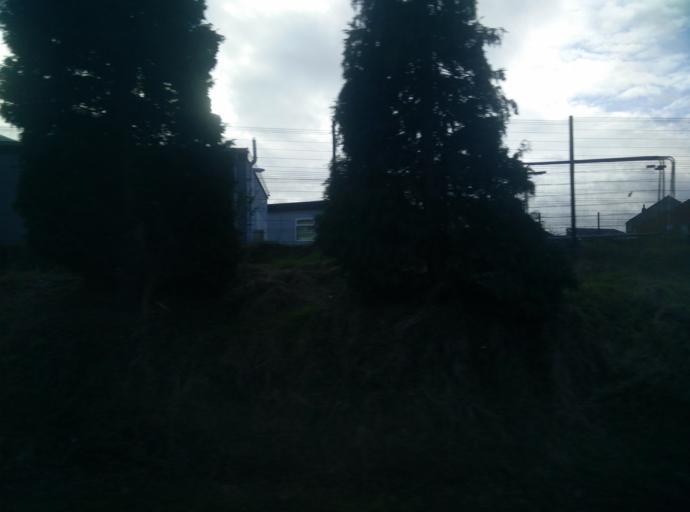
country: GB
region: Northern Ireland
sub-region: City of Belfast
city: Belfast
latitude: 54.5887
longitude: -5.9240
